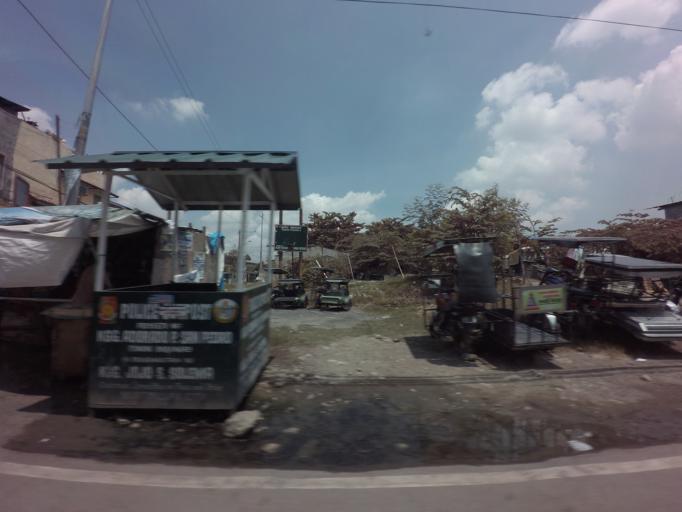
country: PH
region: Calabarzon
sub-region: Province of Laguna
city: San Pedro
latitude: 14.4044
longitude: 121.0502
